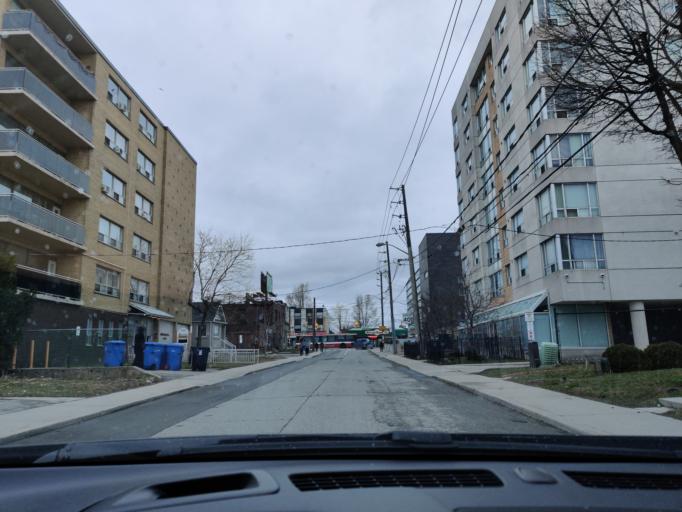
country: CA
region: Ontario
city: Toronto
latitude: 43.6953
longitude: -79.4473
